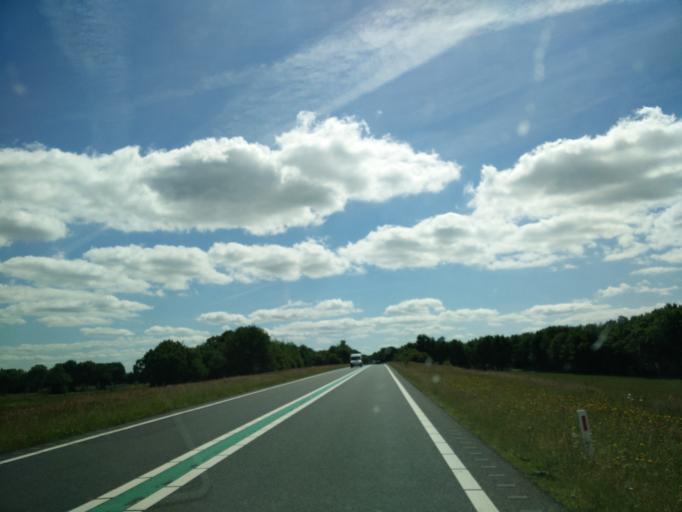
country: NL
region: Drenthe
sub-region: Gemeente Coevorden
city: Sleen
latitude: 52.8073
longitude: 6.6979
